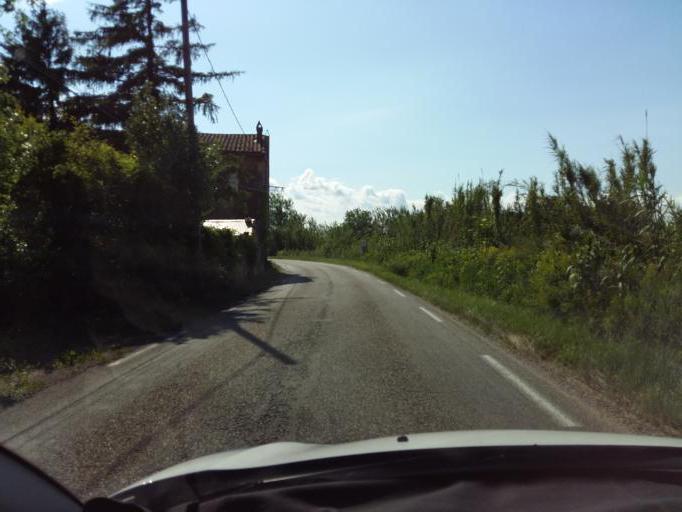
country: FR
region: Provence-Alpes-Cote d'Azur
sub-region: Departement du Vaucluse
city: Taillades
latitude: 43.8504
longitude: 5.0646
